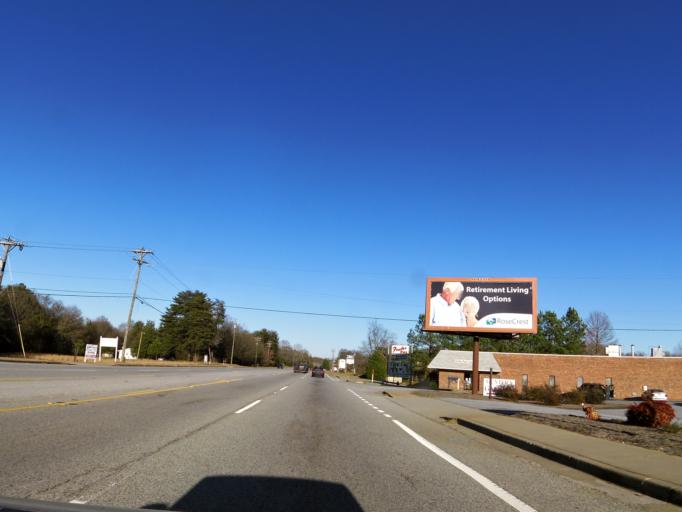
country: US
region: South Carolina
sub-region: Spartanburg County
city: Fairforest
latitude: 34.9083
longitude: -82.0201
